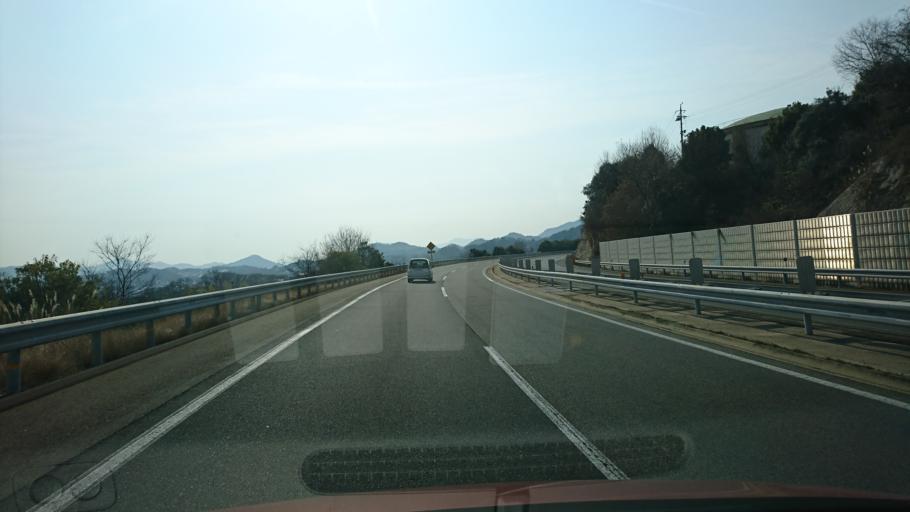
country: JP
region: Hiroshima
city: Onomichi
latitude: 34.4162
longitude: 133.2203
